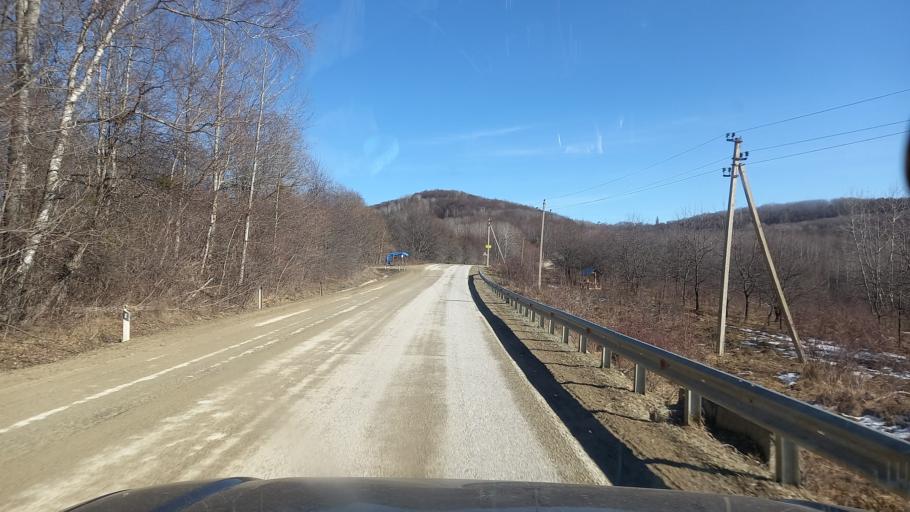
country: RU
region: Adygeya
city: Kamennomostskiy
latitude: 44.2859
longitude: 40.2972
